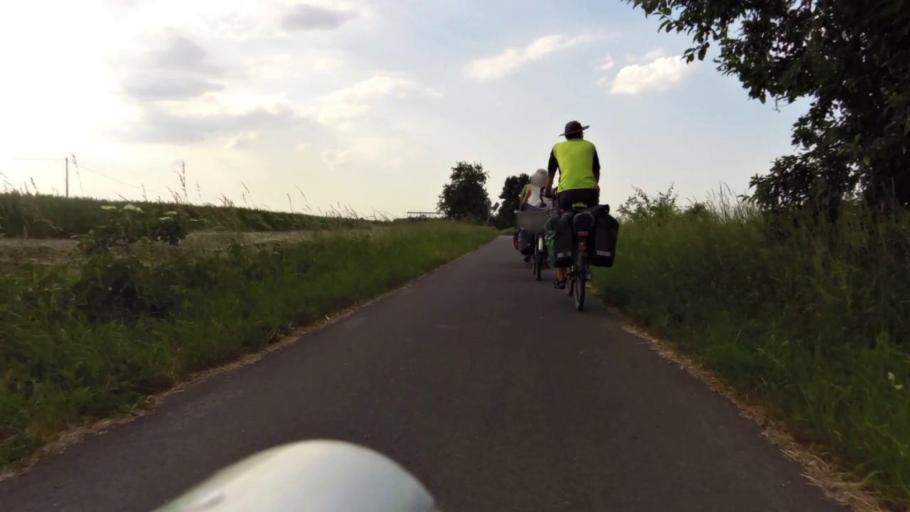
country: PL
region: Kujawsko-Pomorskie
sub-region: Powiat torunski
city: Lubianka
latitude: 53.1252
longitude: 18.4675
